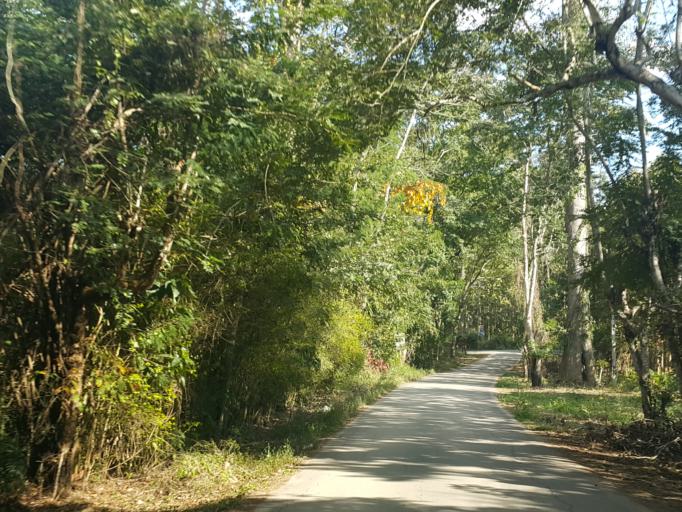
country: TH
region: Chiang Mai
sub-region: Amphoe Chiang Dao
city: Chiang Dao
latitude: 19.4002
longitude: 98.9266
